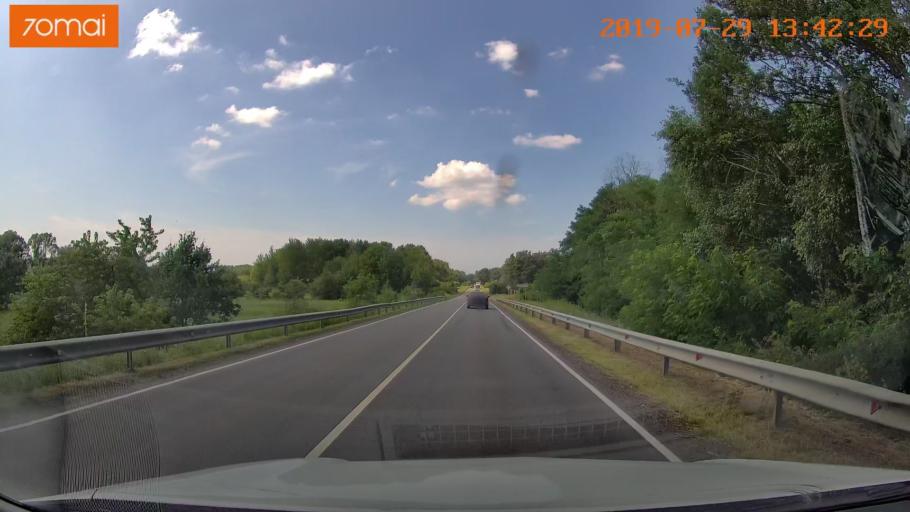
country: RU
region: Kaliningrad
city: Svetlyy
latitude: 54.7368
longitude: 20.1112
